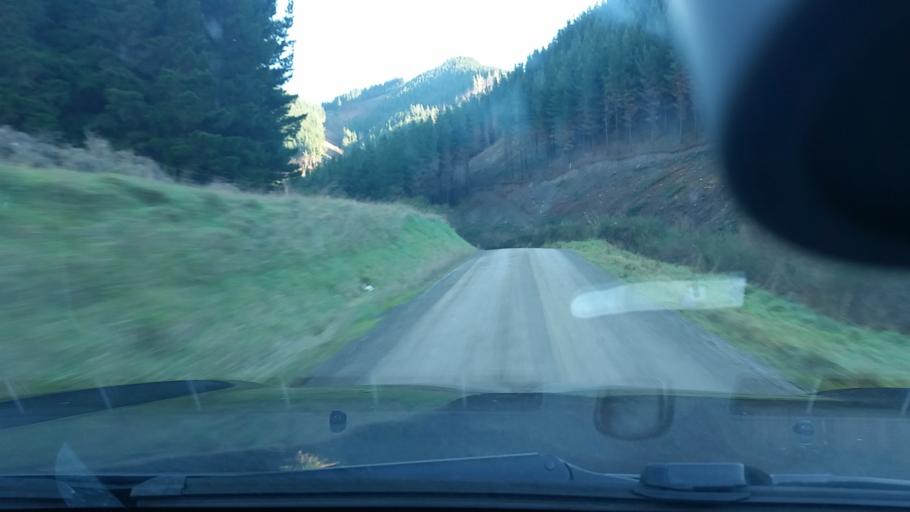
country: NZ
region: Marlborough
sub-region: Marlborough District
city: Blenheim
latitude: -41.6107
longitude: 173.9725
